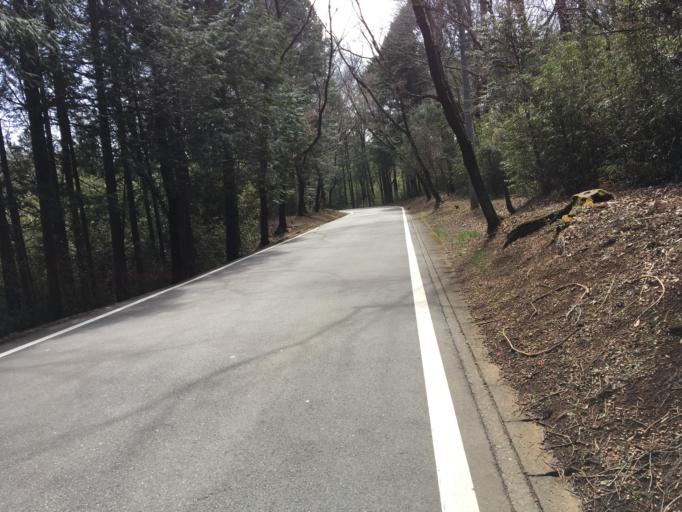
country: JP
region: Saitama
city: Ogawa
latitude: 36.0125
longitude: 139.3274
